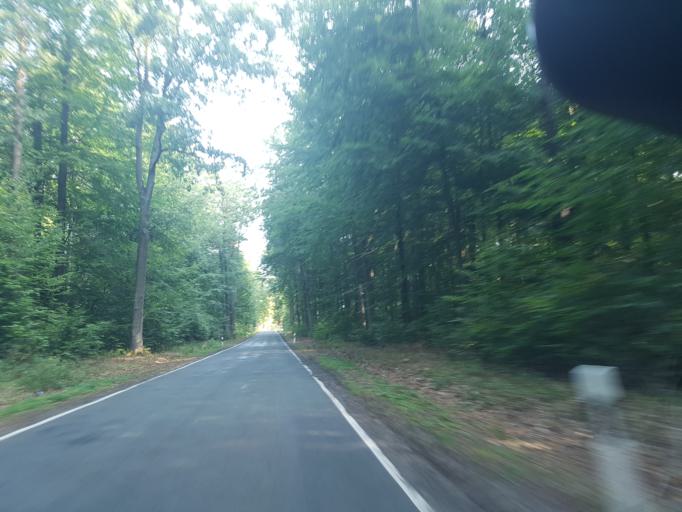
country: DE
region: Brandenburg
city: Wiesenburg
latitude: 52.0431
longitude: 12.3773
